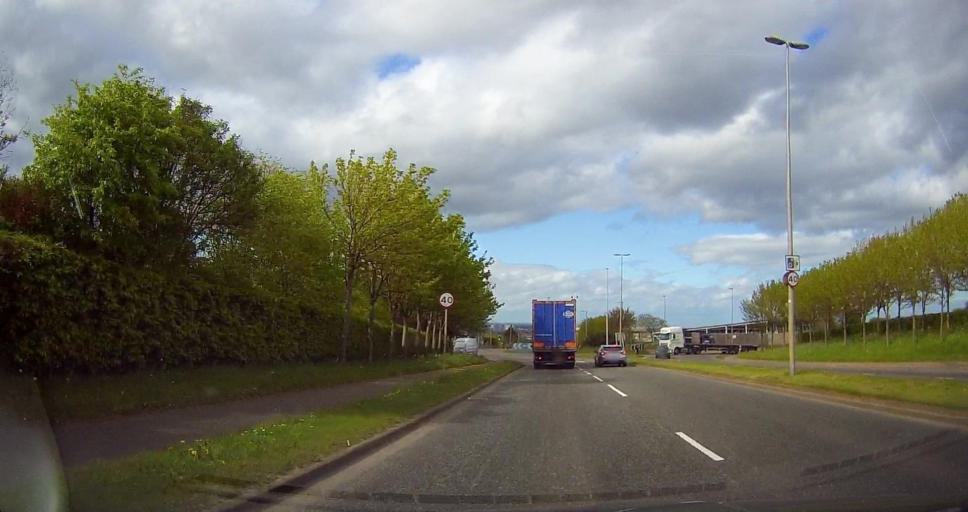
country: GB
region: Scotland
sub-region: Aberdeen City
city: Aberdeen
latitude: 57.1162
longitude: -2.0890
